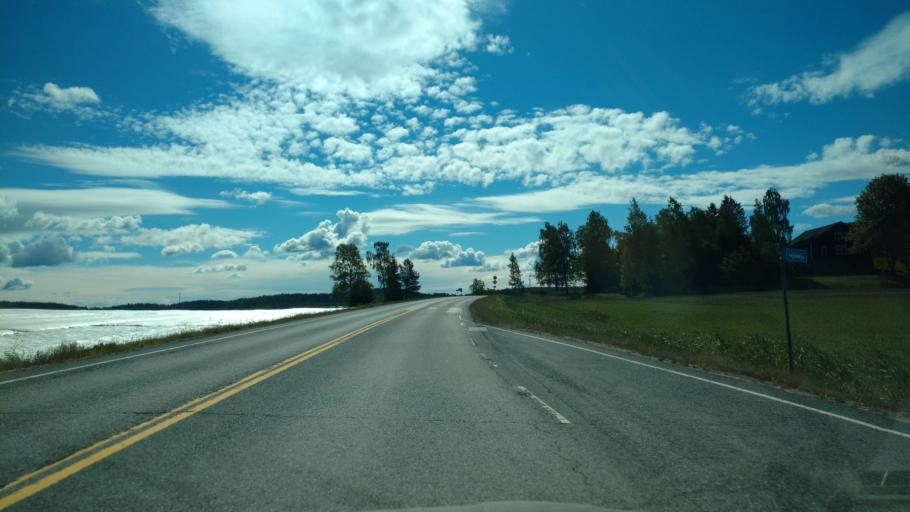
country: FI
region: Varsinais-Suomi
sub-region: Salo
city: Muurla
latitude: 60.3827
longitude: 23.2918
